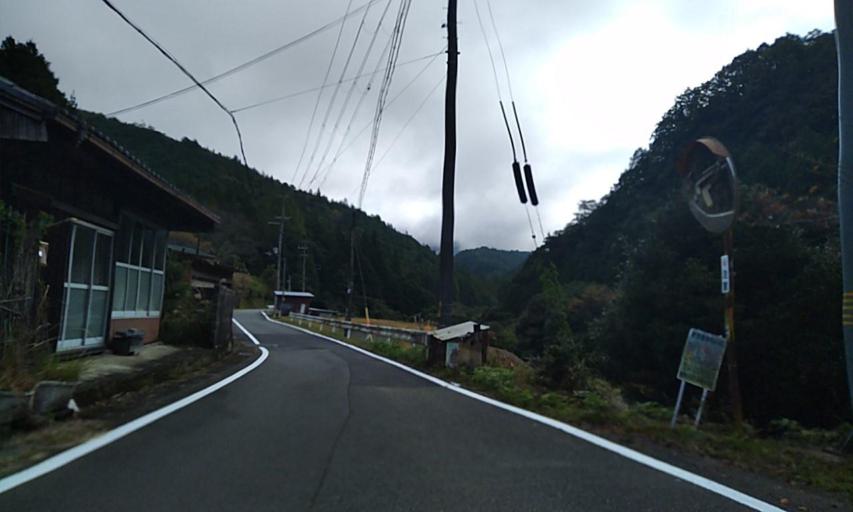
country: JP
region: Wakayama
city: Shingu
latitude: 33.9329
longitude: 135.9750
